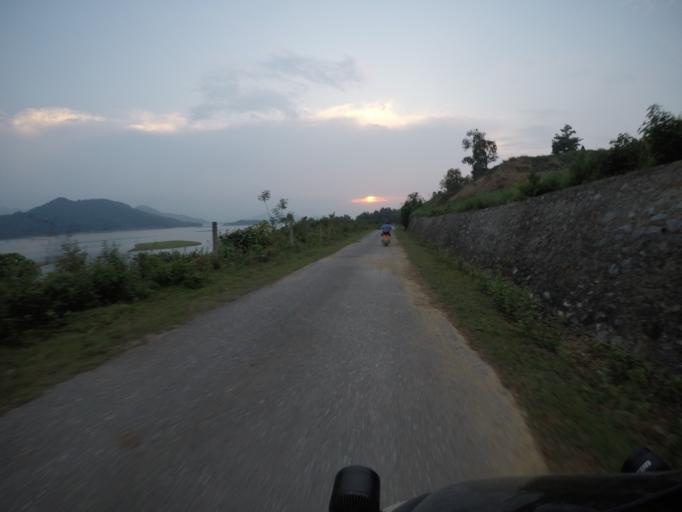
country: VN
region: Thai Nguyen
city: Chua Hang
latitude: 21.5832
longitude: 105.7041
